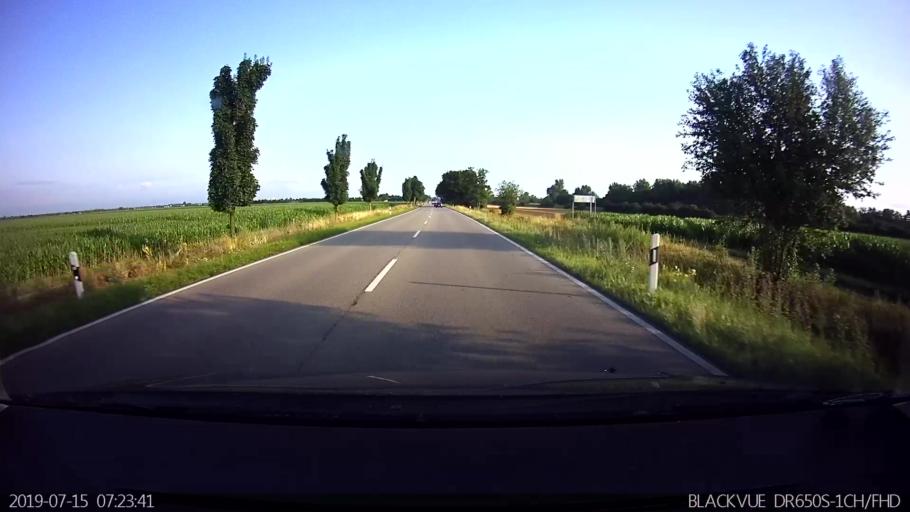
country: DE
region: Baden-Wuerttemberg
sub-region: Freiburg Region
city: Unterkrozingen
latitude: 47.9456
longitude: 7.6757
